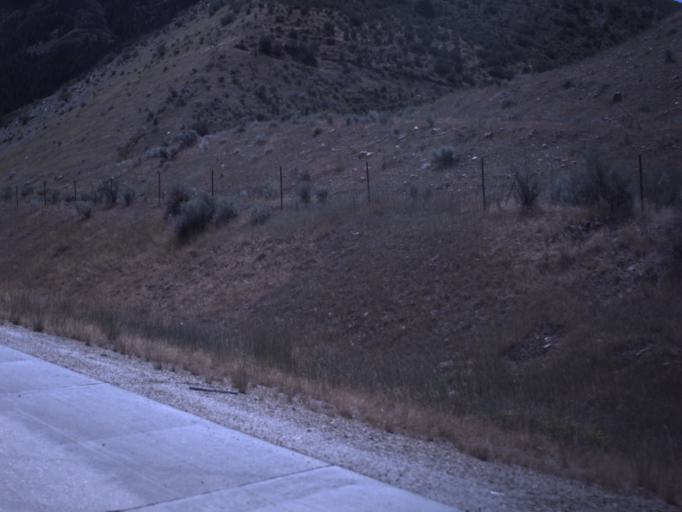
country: US
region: Utah
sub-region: Morgan County
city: Morgan
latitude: 41.0607
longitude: -111.5427
